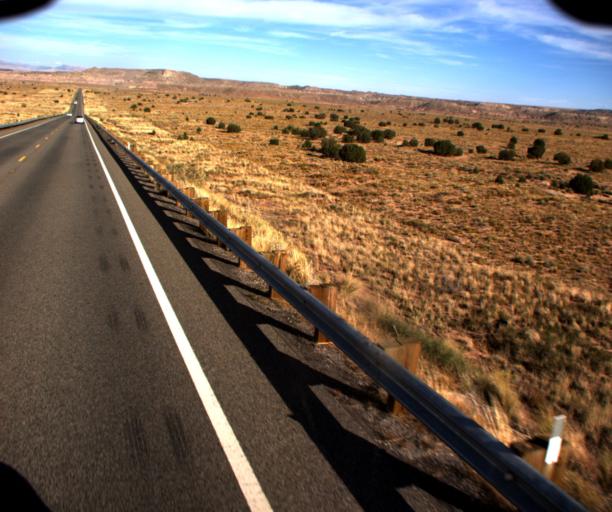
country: US
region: New Mexico
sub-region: San Juan County
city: Shiprock
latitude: 36.9297
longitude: -109.1560
